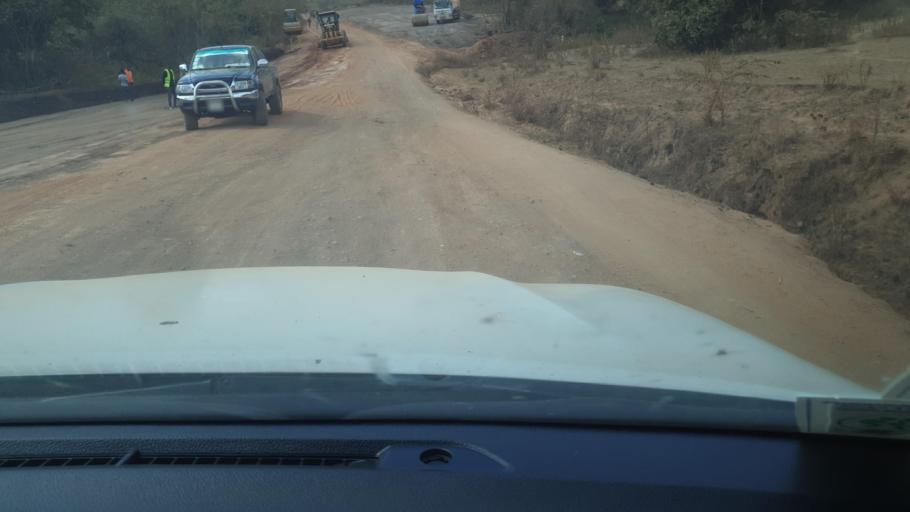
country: ET
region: Oromiya
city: Shakiso
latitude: 5.6098
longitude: 39.0346
